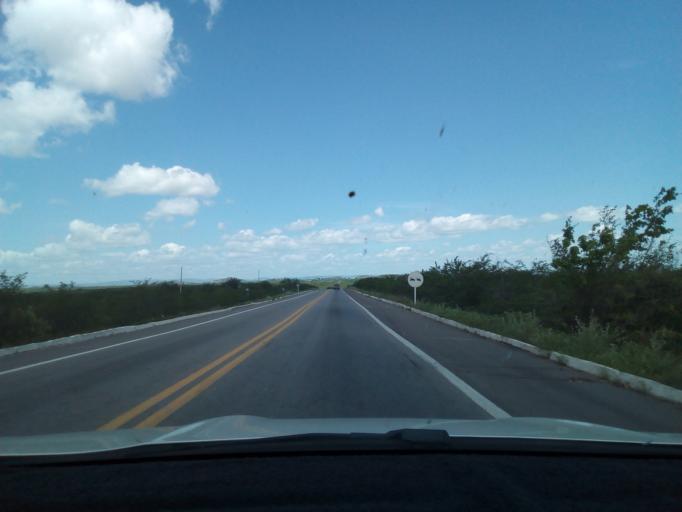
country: BR
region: Rio Grande do Norte
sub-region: Angicos
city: Angicos
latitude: -5.6838
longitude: -36.6008
